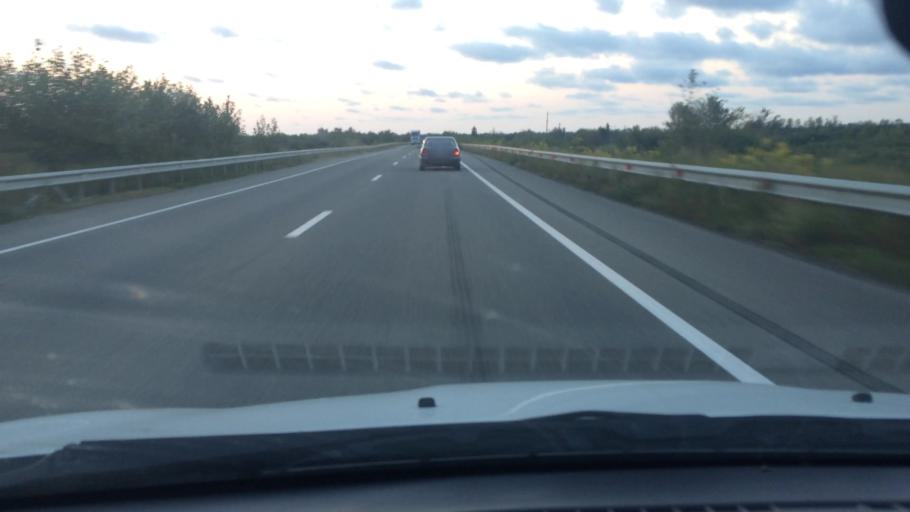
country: GE
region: Ajaria
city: Ochkhamuri
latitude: 41.9056
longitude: 41.7885
